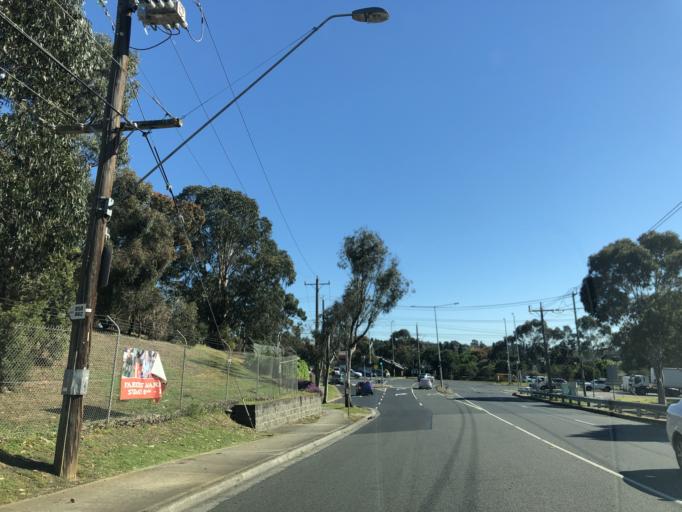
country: AU
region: Victoria
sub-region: Monash
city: Mulgrave
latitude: -37.9243
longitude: 145.1952
